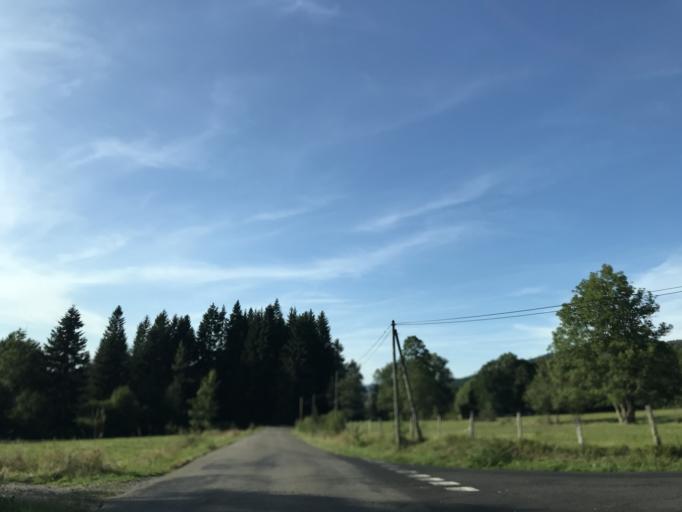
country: FR
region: Auvergne
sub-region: Departement du Puy-de-Dome
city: Job
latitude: 45.6850
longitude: 3.7327
